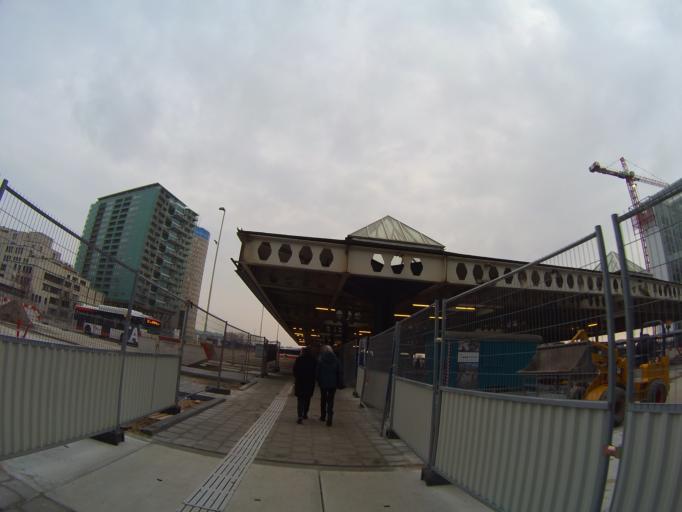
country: NL
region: South Holland
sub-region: Gemeente Den Haag
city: The Hague
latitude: 52.0807
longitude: 4.3248
